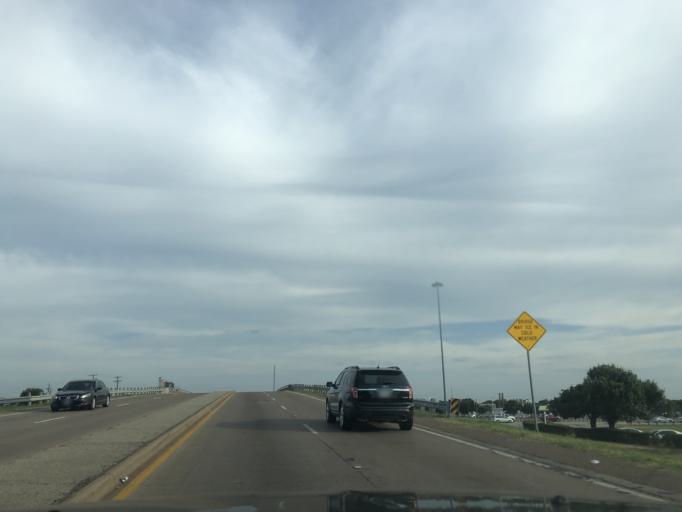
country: US
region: Texas
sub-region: Dallas County
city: Balch Springs
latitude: 32.7968
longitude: -96.6925
